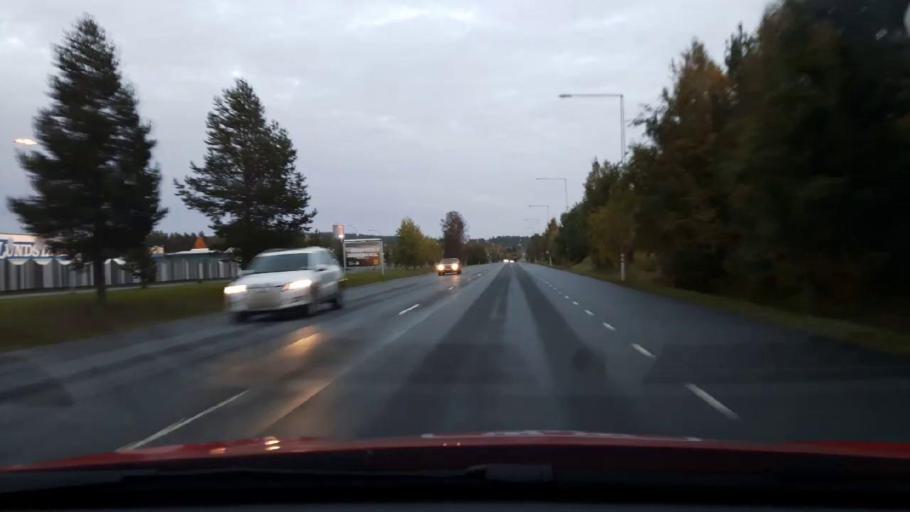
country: SE
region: Jaemtland
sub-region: OEstersunds Kommun
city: Ostersund
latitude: 63.2086
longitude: 14.6381
